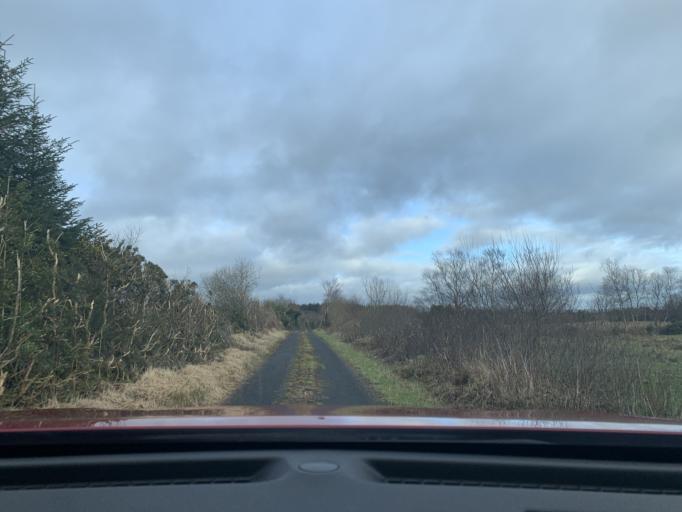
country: IE
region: Connaught
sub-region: Roscommon
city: Ballaghaderreen
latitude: 53.9284
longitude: -8.5601
